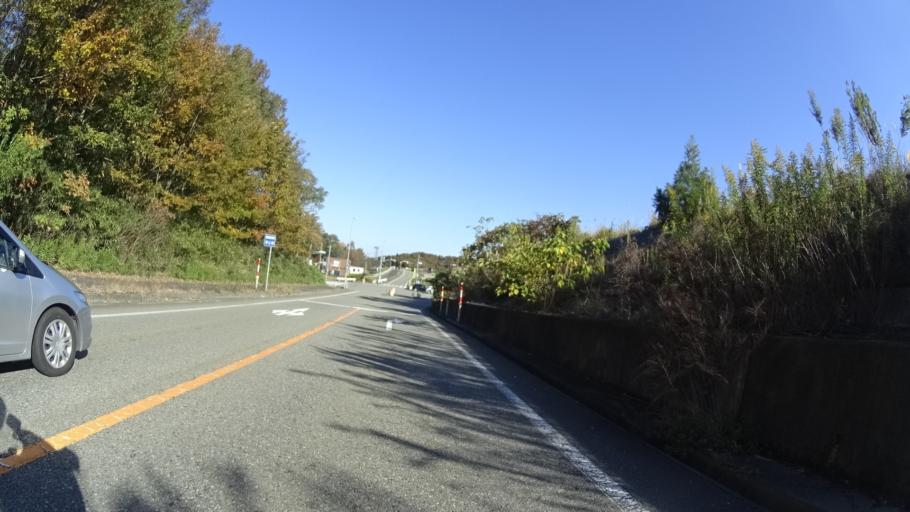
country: JP
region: Ishikawa
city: Komatsu
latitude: 36.3888
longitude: 136.4927
